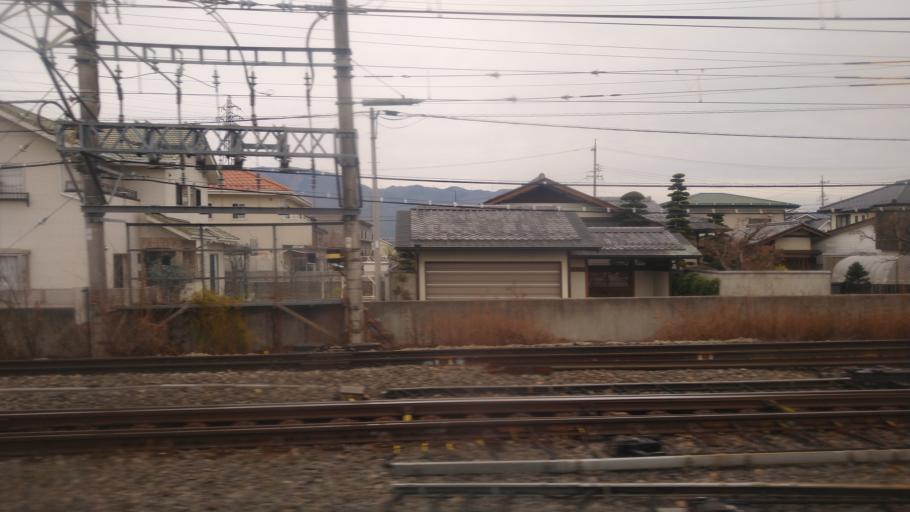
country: JP
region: Nagano
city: Shiojiri
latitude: 36.1180
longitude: 137.9480
